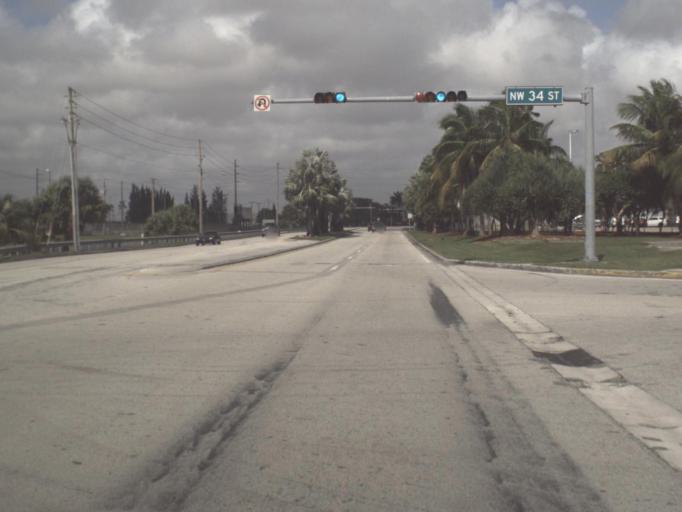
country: US
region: Florida
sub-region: Miami-Dade County
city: Virginia Gardens
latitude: 25.8039
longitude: -80.3049
